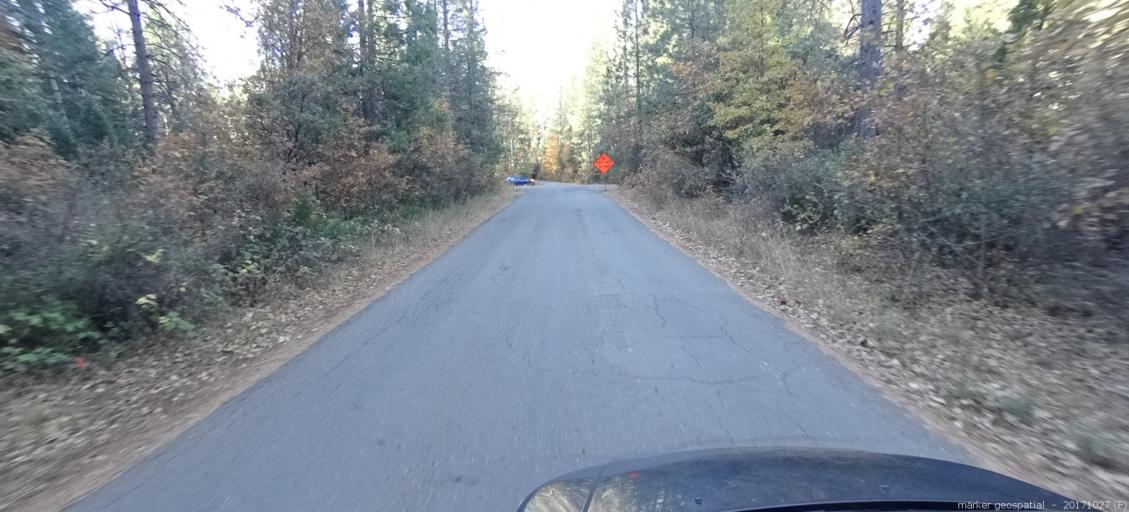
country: US
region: California
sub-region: Shasta County
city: Burney
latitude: 40.9328
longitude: -121.9472
